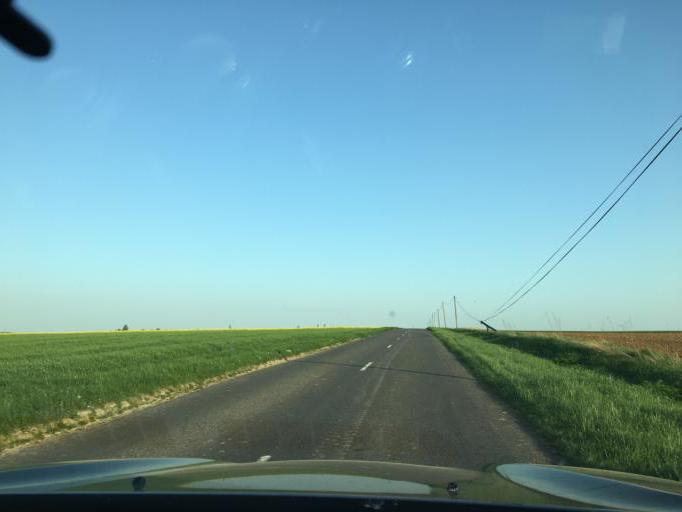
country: FR
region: Centre
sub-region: Departement du Loir-et-Cher
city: Ouzouer-le-Marche
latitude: 47.8499
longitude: 1.5274
